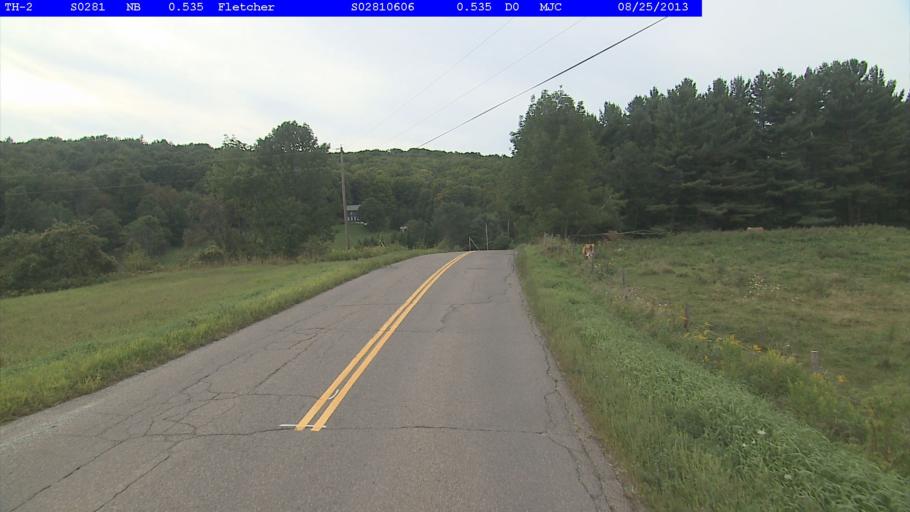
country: US
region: Vermont
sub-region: Chittenden County
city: Milton
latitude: 44.6870
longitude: -72.9237
